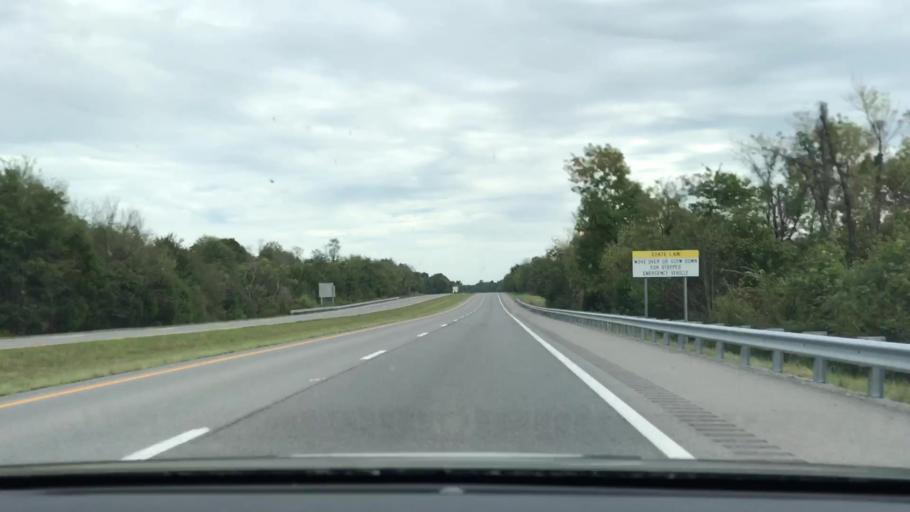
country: US
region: Kentucky
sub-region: Graves County
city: Mayfield
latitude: 36.7784
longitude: -88.5765
